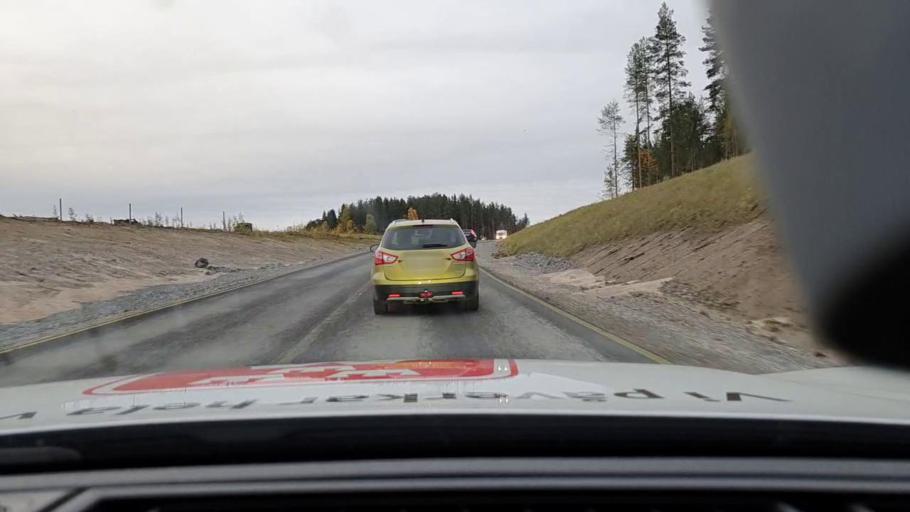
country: SE
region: Norrbotten
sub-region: Bodens Kommun
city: Saevast
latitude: 65.7522
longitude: 21.7640
